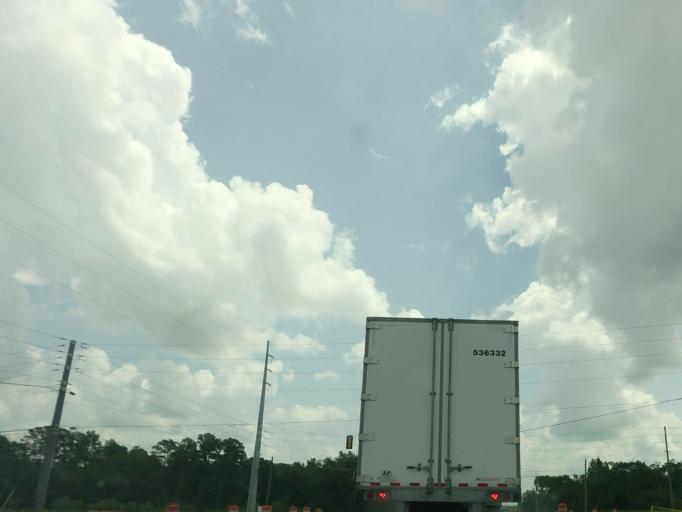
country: US
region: Georgia
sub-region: Houston County
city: Perry
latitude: 32.5465
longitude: -83.7205
